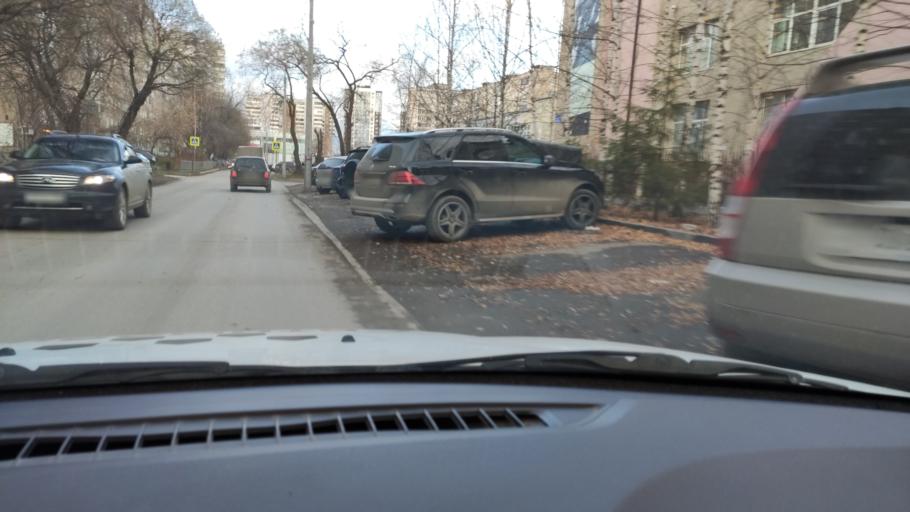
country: RU
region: Perm
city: Kondratovo
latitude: 57.9951
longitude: 56.1564
